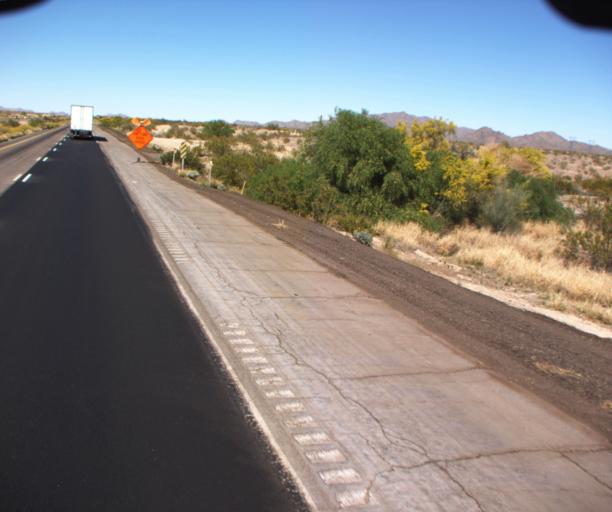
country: US
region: Arizona
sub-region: Maricopa County
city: Gila Bend
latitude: 33.0782
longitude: -112.6467
